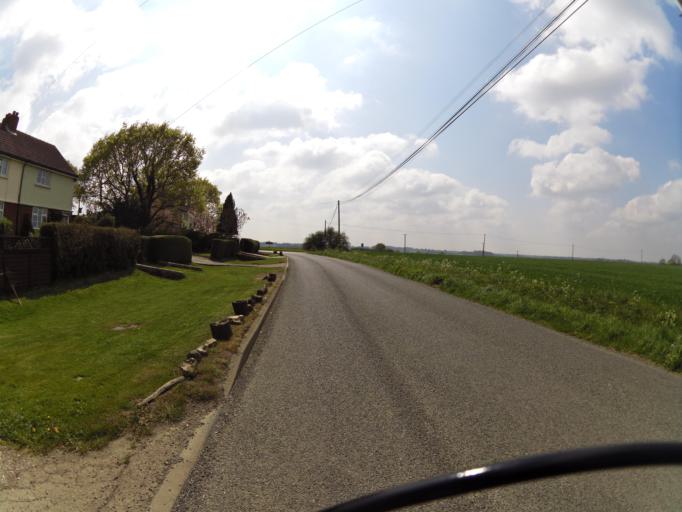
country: GB
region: England
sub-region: Suffolk
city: Hadleigh
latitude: 52.0623
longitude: 0.9517
